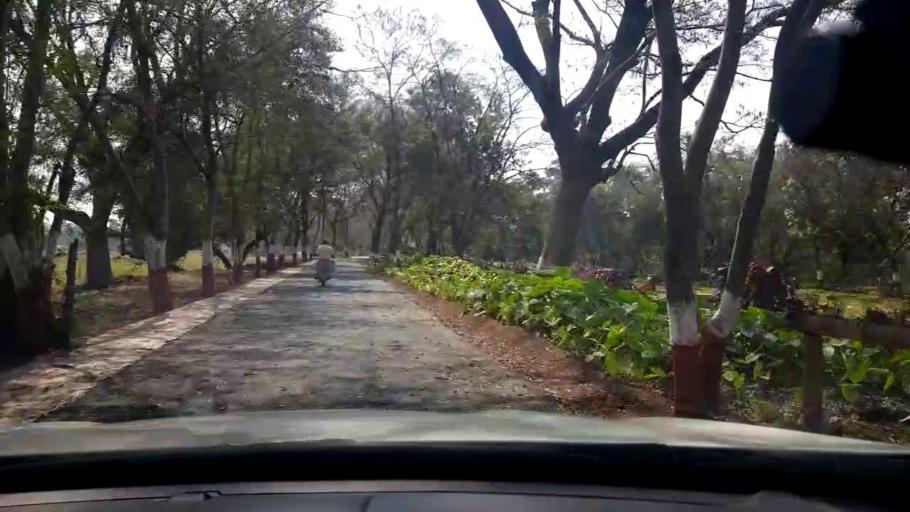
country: IN
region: Maharashtra
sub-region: Pune Division
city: Shivaji Nagar
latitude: 18.5454
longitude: 73.8566
